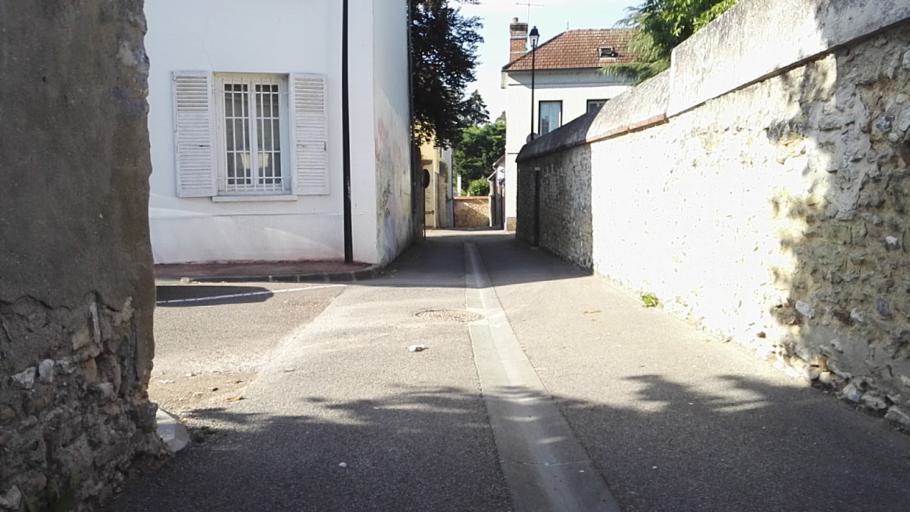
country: FR
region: Haute-Normandie
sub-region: Departement de l'Eure
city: Pacy-sur-Eure
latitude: 49.0154
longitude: 1.3816
